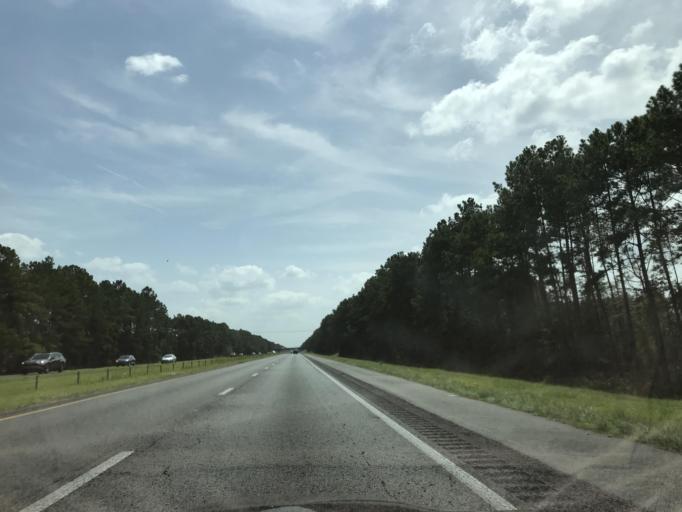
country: US
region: North Carolina
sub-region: Duplin County
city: Wallace
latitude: 34.7416
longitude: -77.9446
